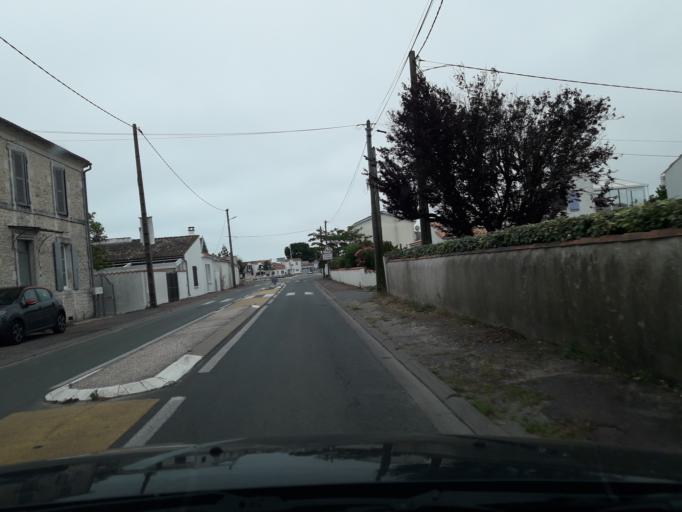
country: FR
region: Poitou-Charentes
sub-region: Departement de la Charente-Maritime
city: Boyard-Ville
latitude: 45.9653
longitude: -1.2456
